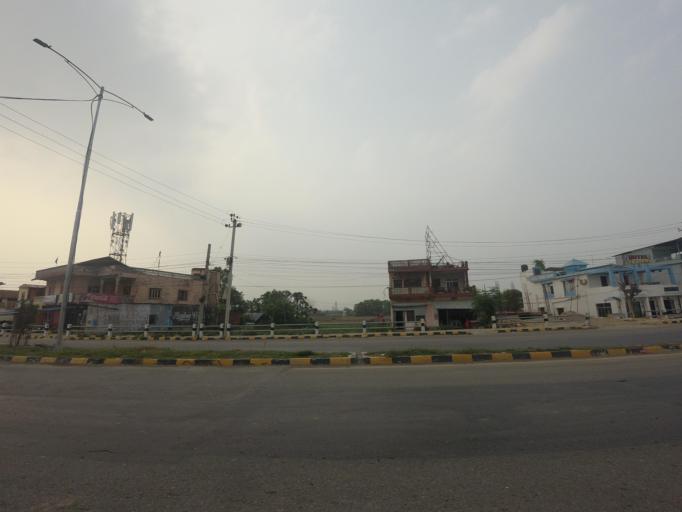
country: NP
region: Western Region
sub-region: Lumbini Zone
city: Bhairahawa
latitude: 27.5095
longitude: 83.4183
